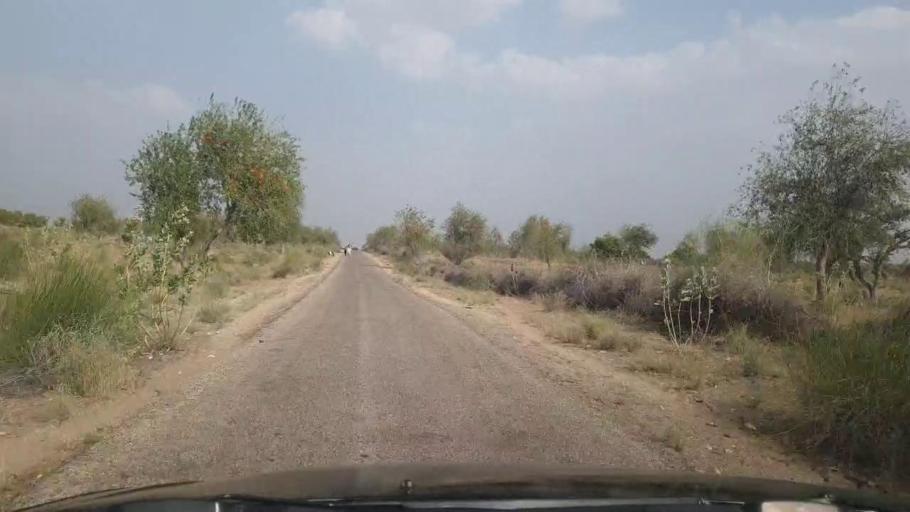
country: PK
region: Sindh
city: Islamkot
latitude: 25.0245
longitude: 70.5618
